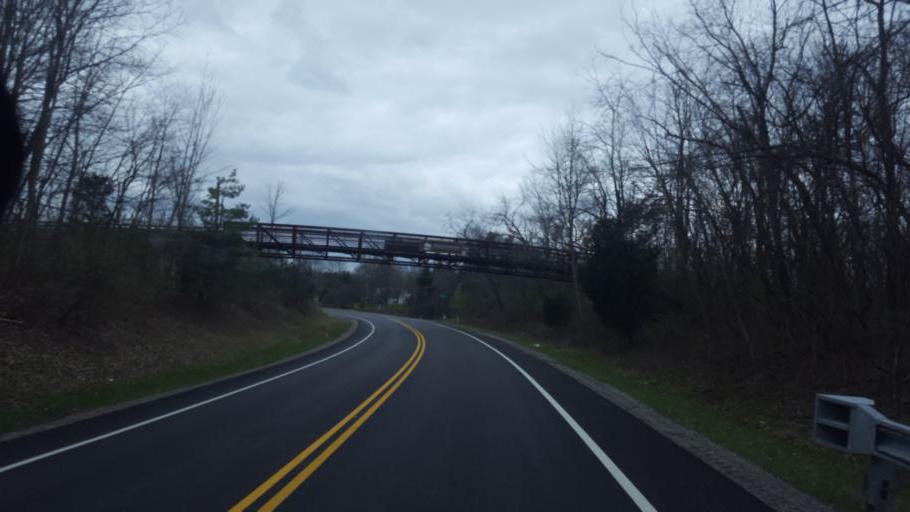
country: US
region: Ohio
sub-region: Delaware County
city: Sunbury
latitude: 40.2086
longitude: -82.8947
